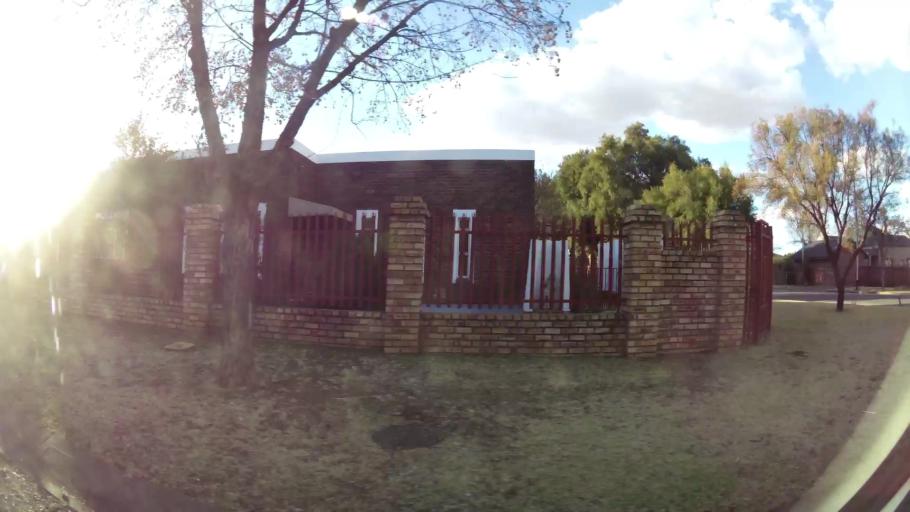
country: ZA
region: North-West
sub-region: Dr Kenneth Kaunda District Municipality
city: Potchefstroom
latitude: -26.7240
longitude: 27.0846
